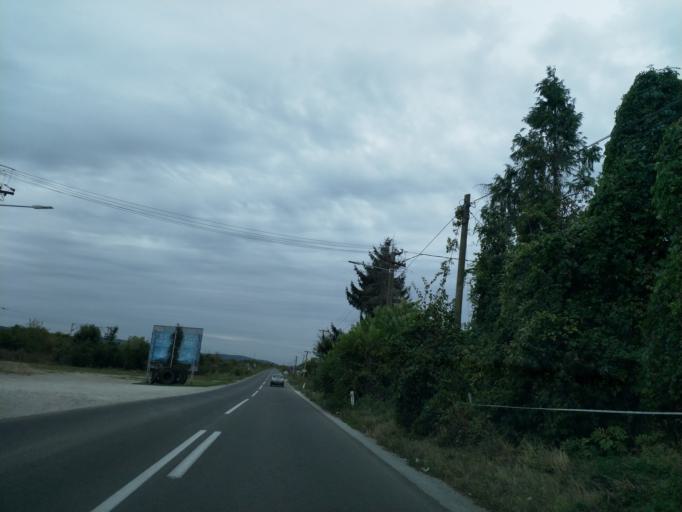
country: RS
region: Central Serbia
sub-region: Sumadijski Okrug
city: Batocina
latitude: 44.1476
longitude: 21.1098
